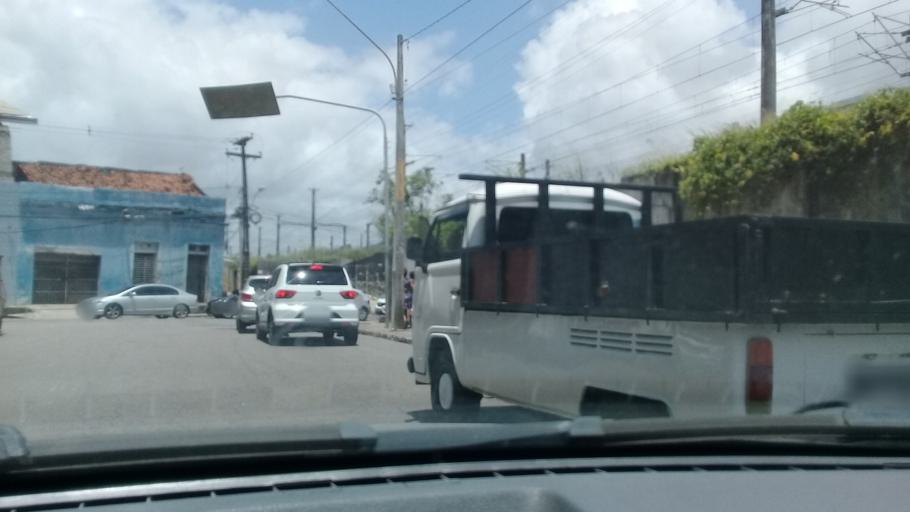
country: BR
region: Pernambuco
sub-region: Recife
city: Recife
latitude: -8.0731
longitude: -34.8903
